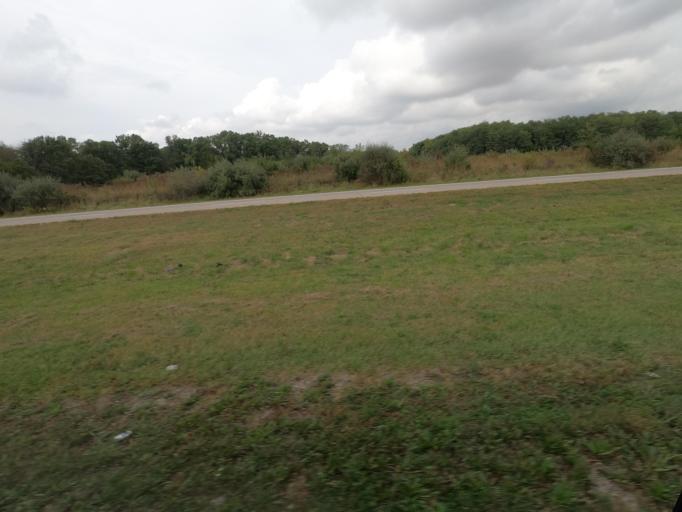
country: US
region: Iowa
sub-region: Wapello County
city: Ottumwa
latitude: 40.9983
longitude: -92.3308
